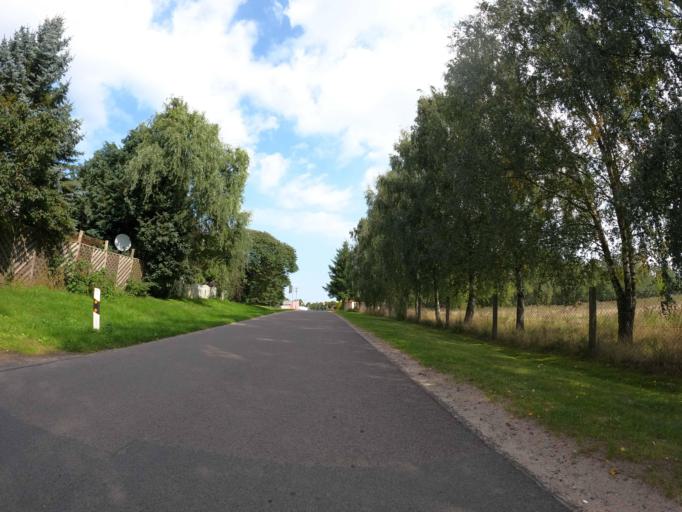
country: DE
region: Mecklenburg-Vorpommern
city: Malchow
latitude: 53.4588
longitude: 12.4811
